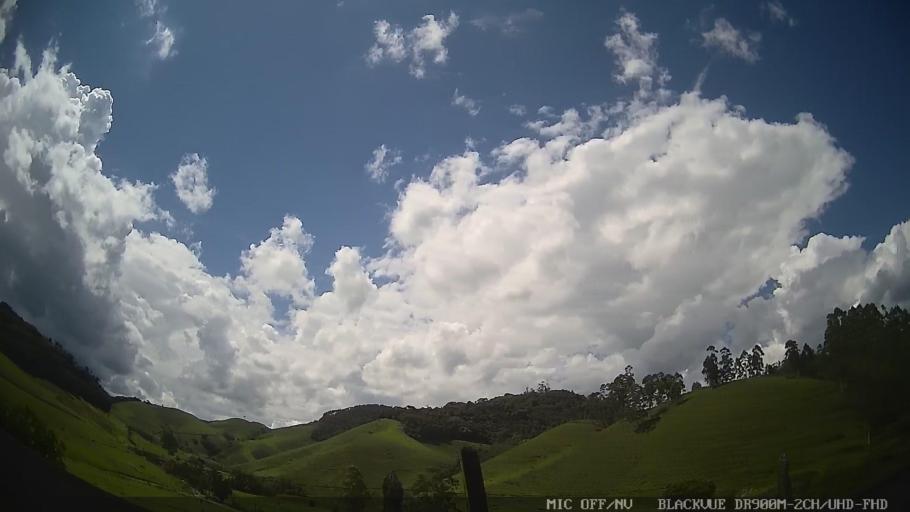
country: BR
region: Sao Paulo
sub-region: Caraguatatuba
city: Caraguatatuba
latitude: -23.5360
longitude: -45.5745
